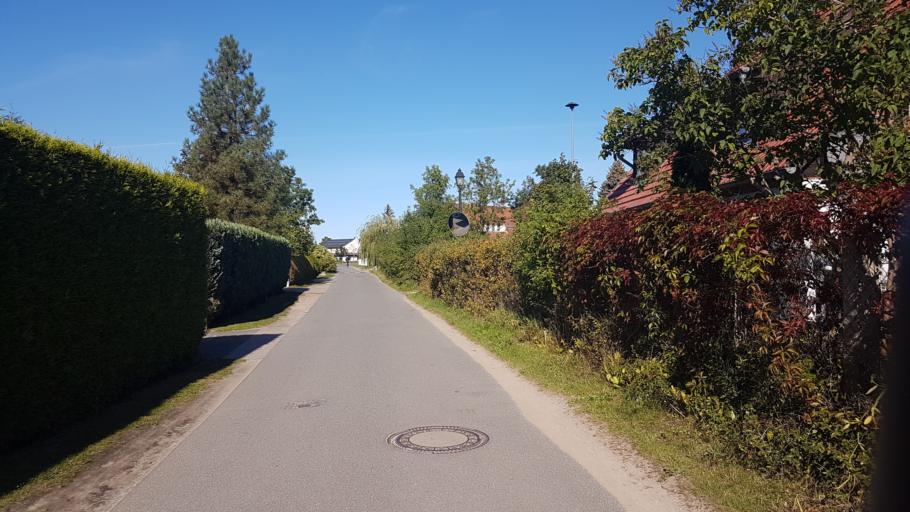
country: DE
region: Mecklenburg-Vorpommern
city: Glowe
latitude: 54.5685
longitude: 13.4730
